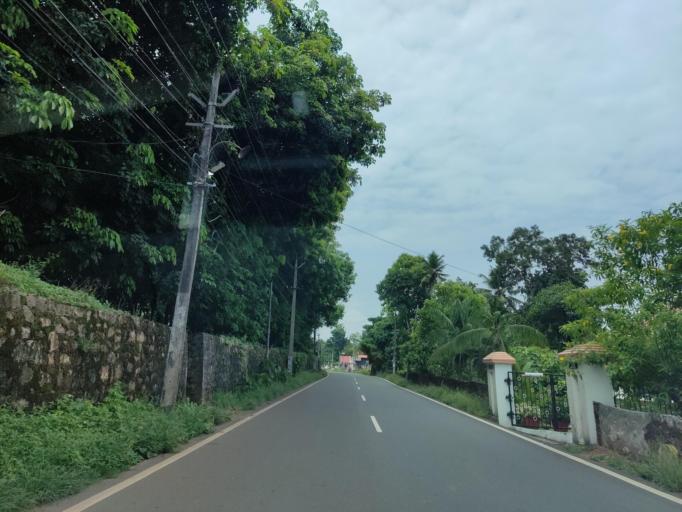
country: IN
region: Kerala
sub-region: Alappuzha
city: Chengannur
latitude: 9.2925
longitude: 76.6199
